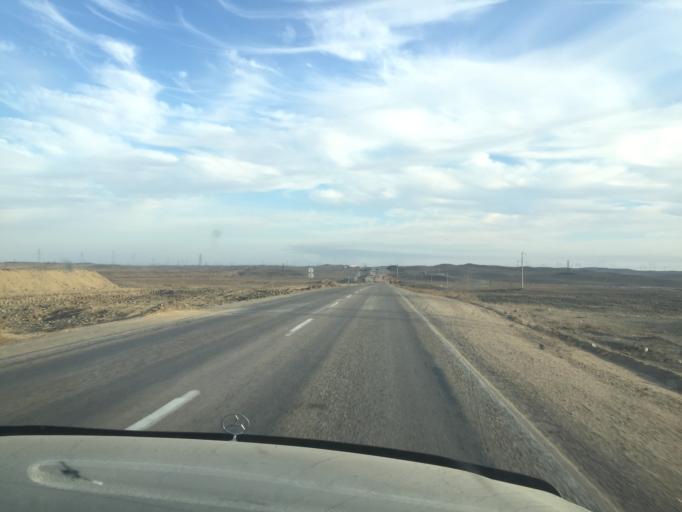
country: KZ
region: Almaty Oblysy
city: Ulken
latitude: 45.2123
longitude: 73.8739
